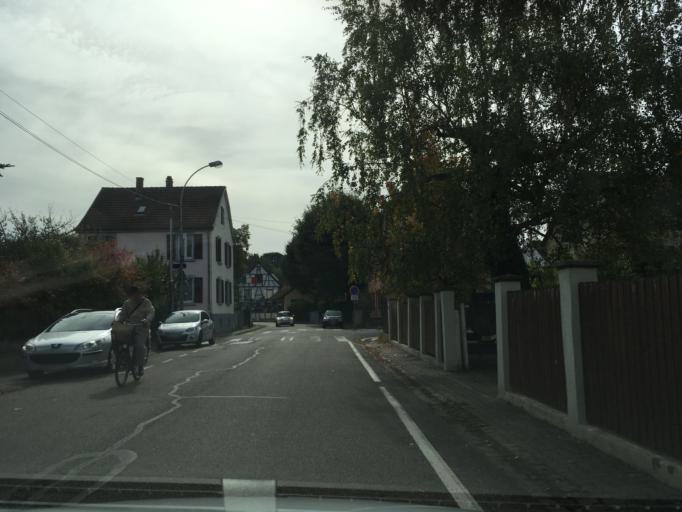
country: FR
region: Alsace
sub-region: Departement du Bas-Rhin
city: Bischheim
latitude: 48.5975
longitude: 7.7849
